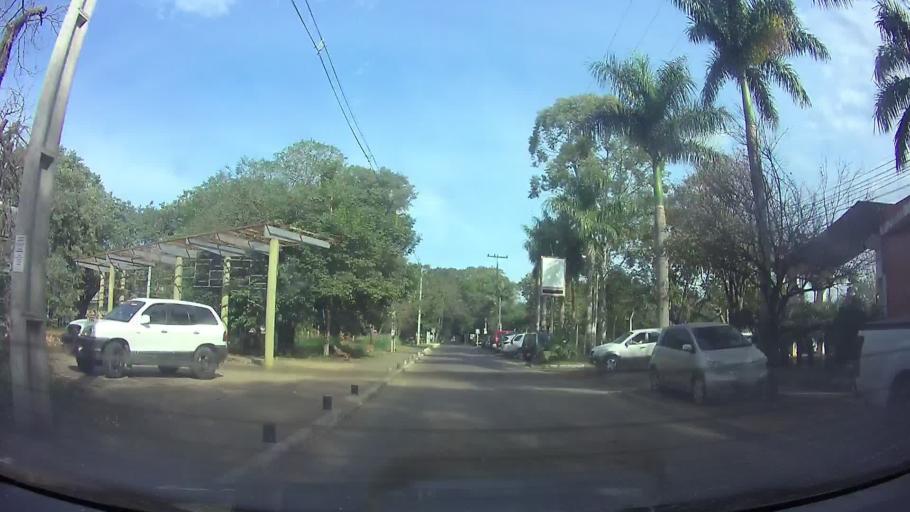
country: PY
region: Central
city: Fernando de la Mora
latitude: -25.3328
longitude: -57.5167
